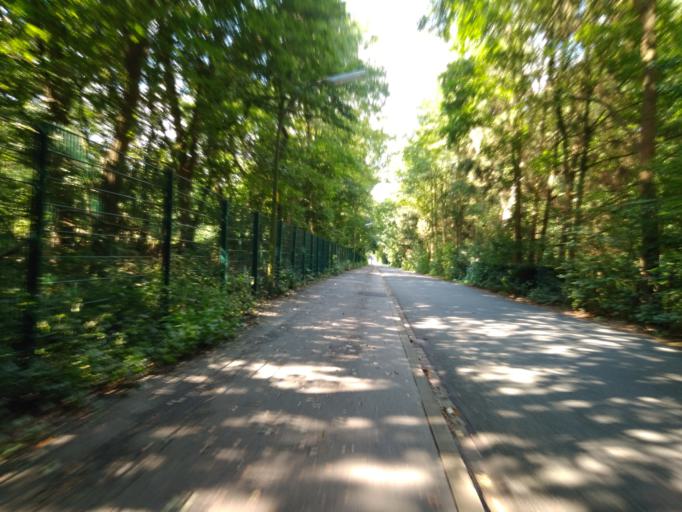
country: DE
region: North Rhine-Westphalia
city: Dorsten
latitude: 51.6830
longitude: 6.9708
